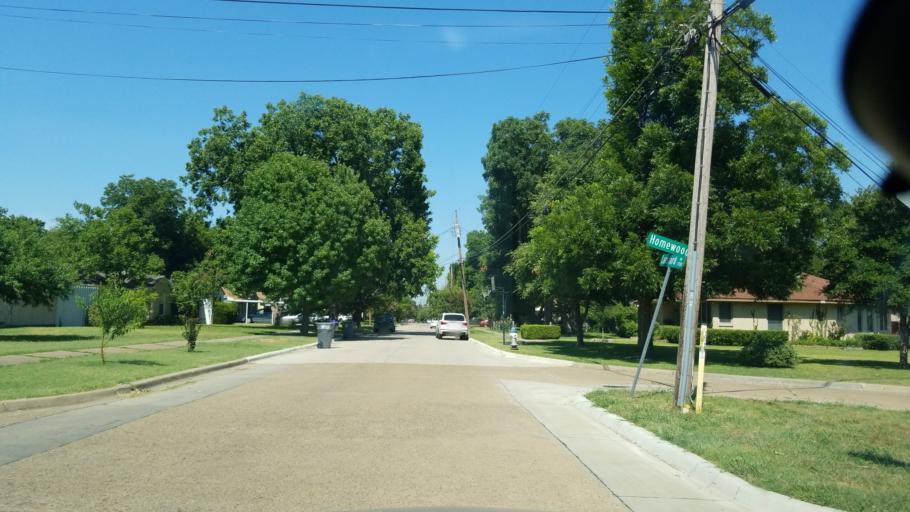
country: US
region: Texas
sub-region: Dallas County
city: Cockrell Hill
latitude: 32.7288
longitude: -96.8493
